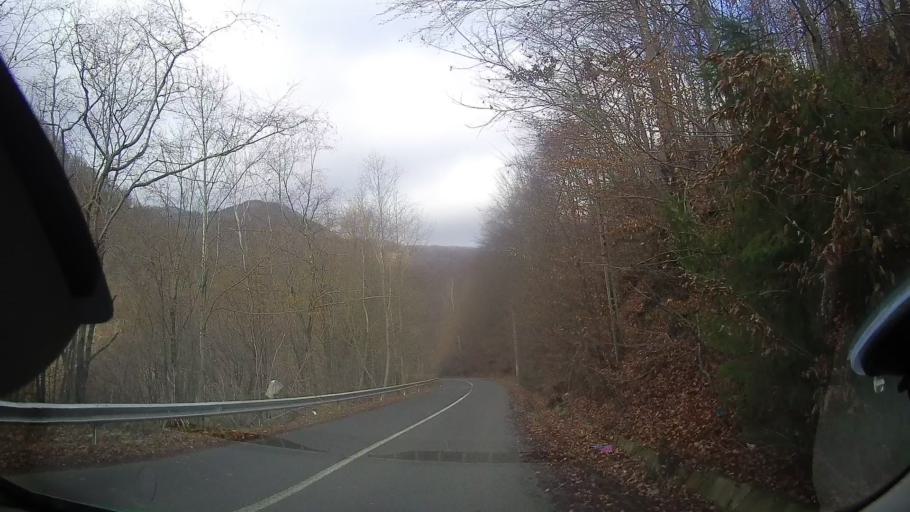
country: RO
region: Cluj
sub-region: Comuna Valea Ierii
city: Valea Ierii
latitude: 46.6866
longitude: 23.3067
